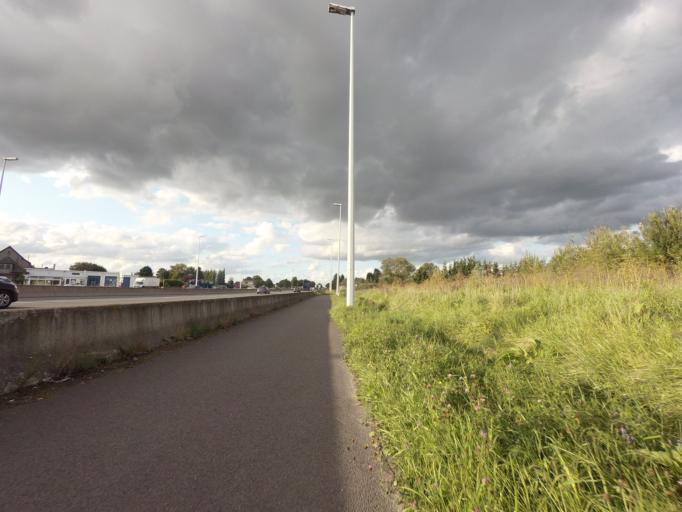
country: BE
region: Flanders
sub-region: Provincie Vlaams-Brabant
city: Londerzeel
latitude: 50.9976
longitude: 4.3166
